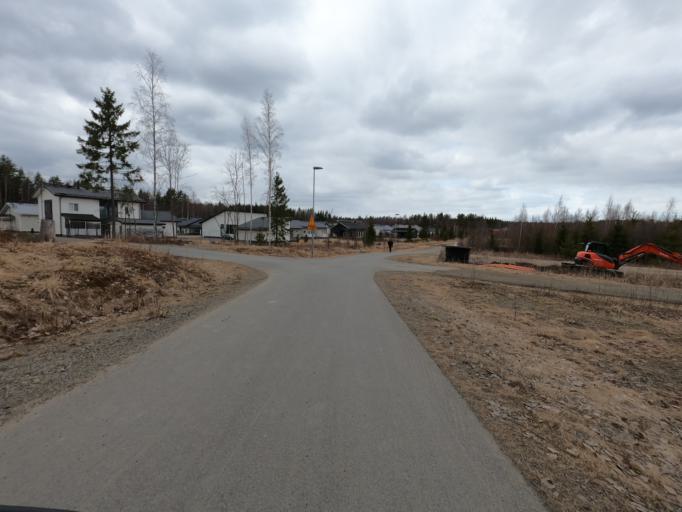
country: FI
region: North Karelia
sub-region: Joensuu
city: Joensuu
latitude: 62.5661
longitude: 29.8187
